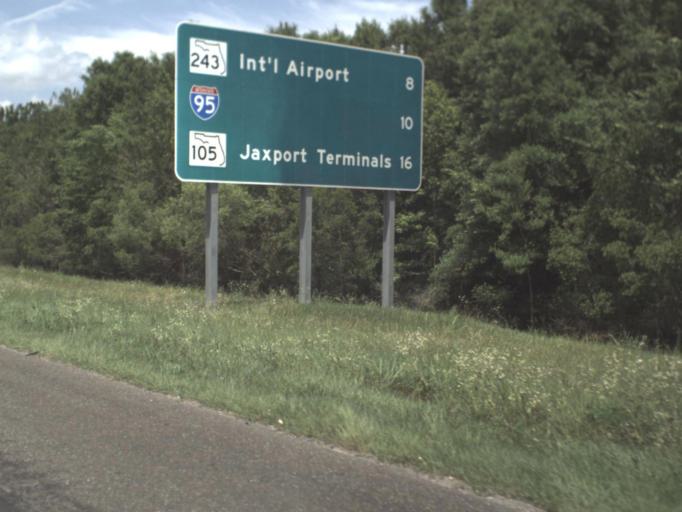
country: US
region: Florida
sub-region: Duval County
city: Jacksonville
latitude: 30.3835
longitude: -81.7599
